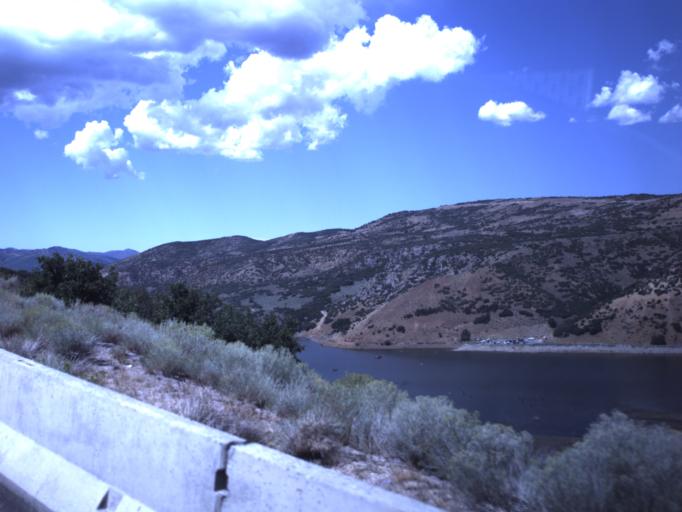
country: US
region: Utah
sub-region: Summit County
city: Francis
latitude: 40.5978
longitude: -111.3455
